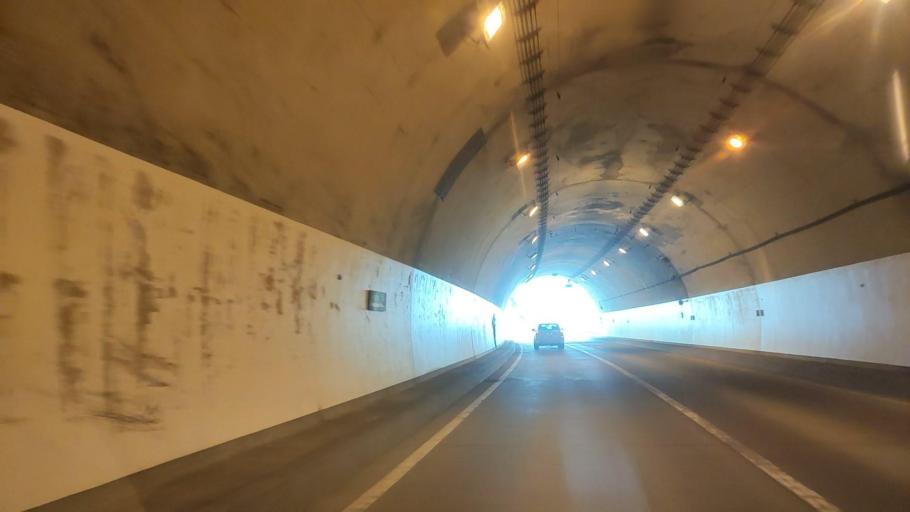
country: JP
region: Hokkaido
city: Ishikari
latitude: 43.4712
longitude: 141.3960
